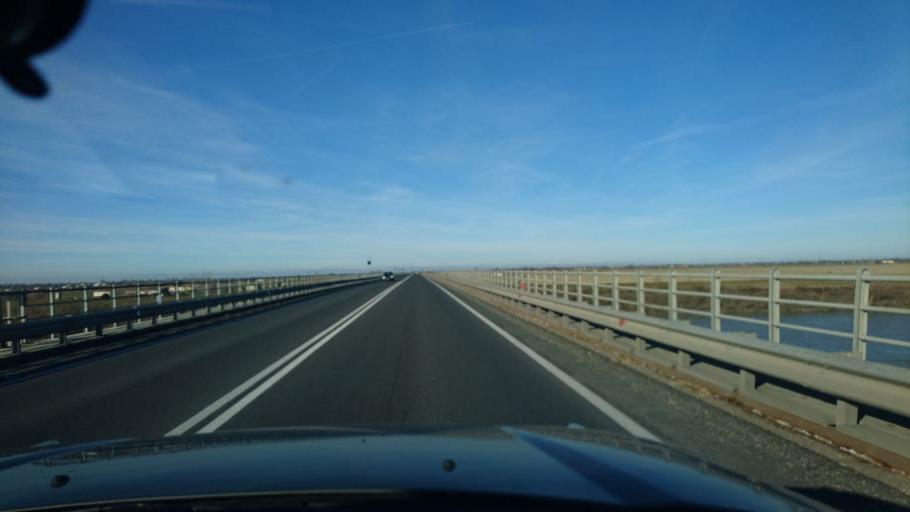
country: IT
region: Veneto
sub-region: Provincia di Rovigo
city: Bottrighe
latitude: 45.0225
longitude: 12.0993
